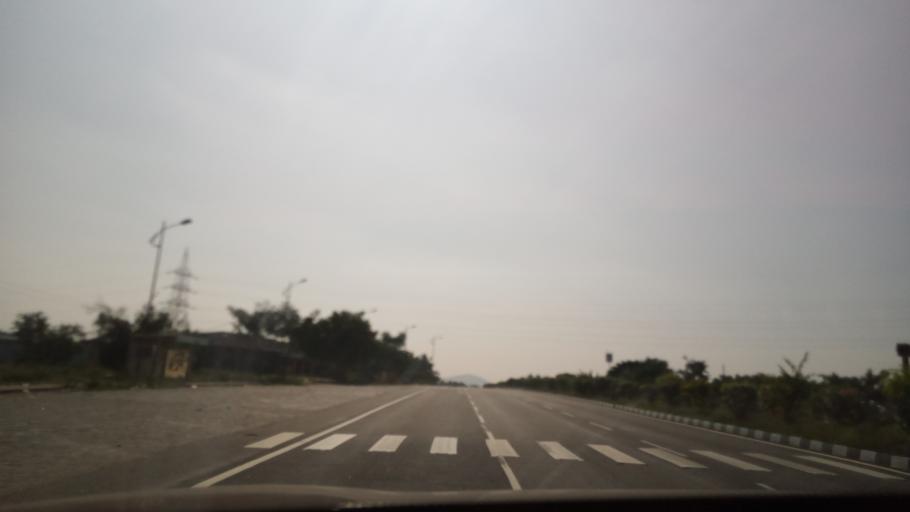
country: IN
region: Tamil Nadu
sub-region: Vellore
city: Jolarpettai
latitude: 12.6013
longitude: 78.5384
